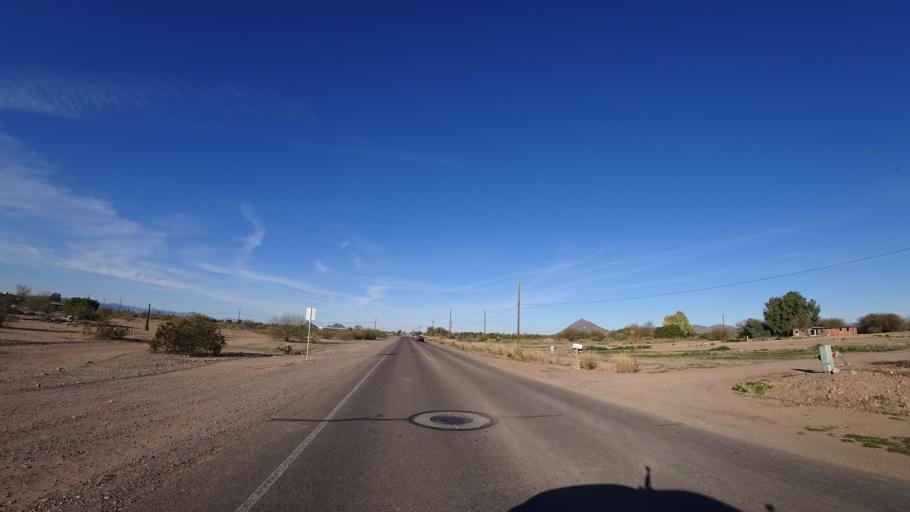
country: US
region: Arizona
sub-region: Maricopa County
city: Scottsdale
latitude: 33.4804
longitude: -111.8806
